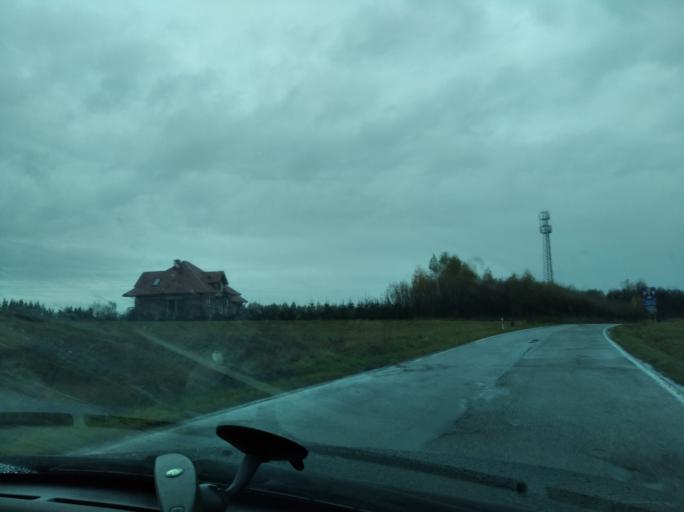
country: PL
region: Subcarpathian Voivodeship
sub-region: Powiat lancucki
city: Handzlowka
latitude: 49.9932
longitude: 22.1919
